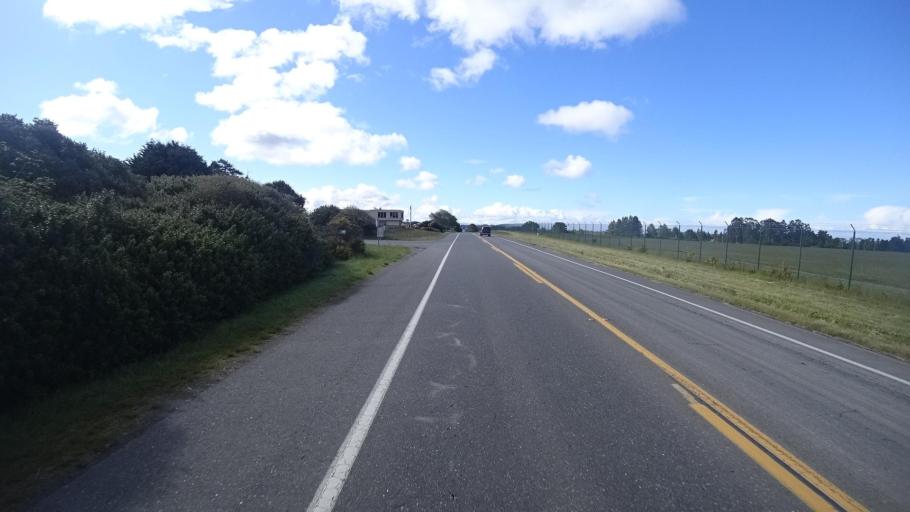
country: US
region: California
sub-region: Humboldt County
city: McKinleyville
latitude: 40.9696
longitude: -124.1006
